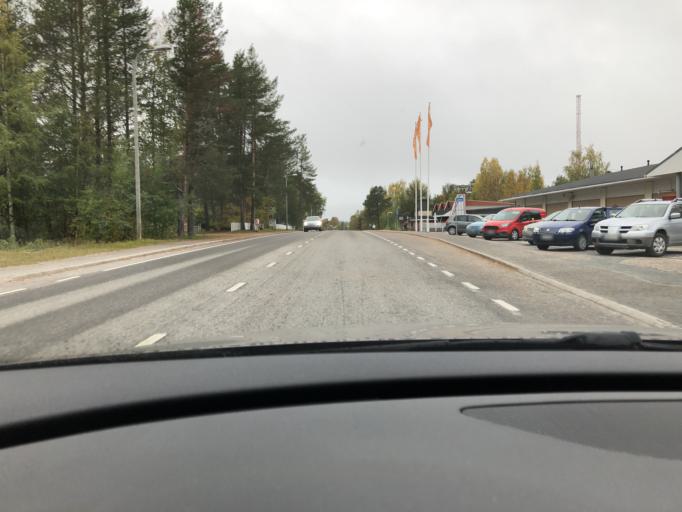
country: FI
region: Lapland
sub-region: Itae-Lappi
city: Posio
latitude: 66.1097
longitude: 28.1724
